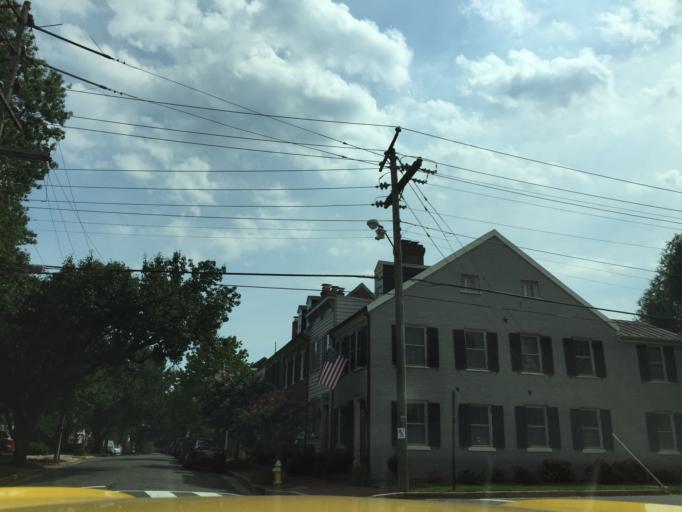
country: US
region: Virginia
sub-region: City of Alexandria
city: Alexandria
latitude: 38.7989
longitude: -77.0427
